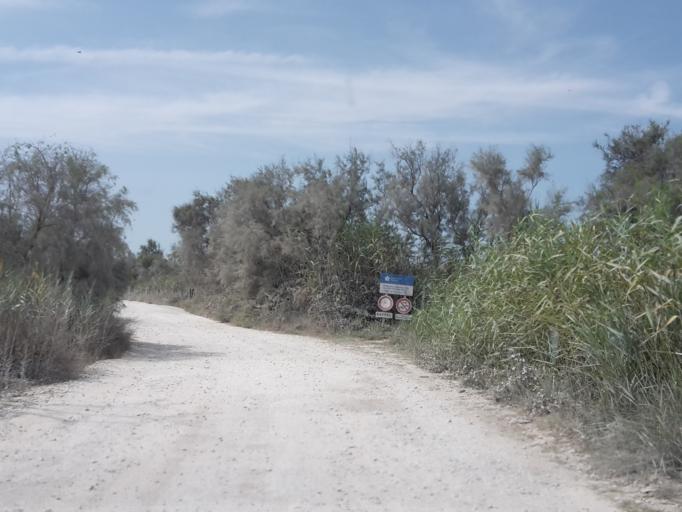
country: FR
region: Provence-Alpes-Cote d'Azur
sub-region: Departement des Bouches-du-Rhone
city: Port-Saint-Louis-du-Rhone
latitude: 43.4136
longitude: 4.6912
